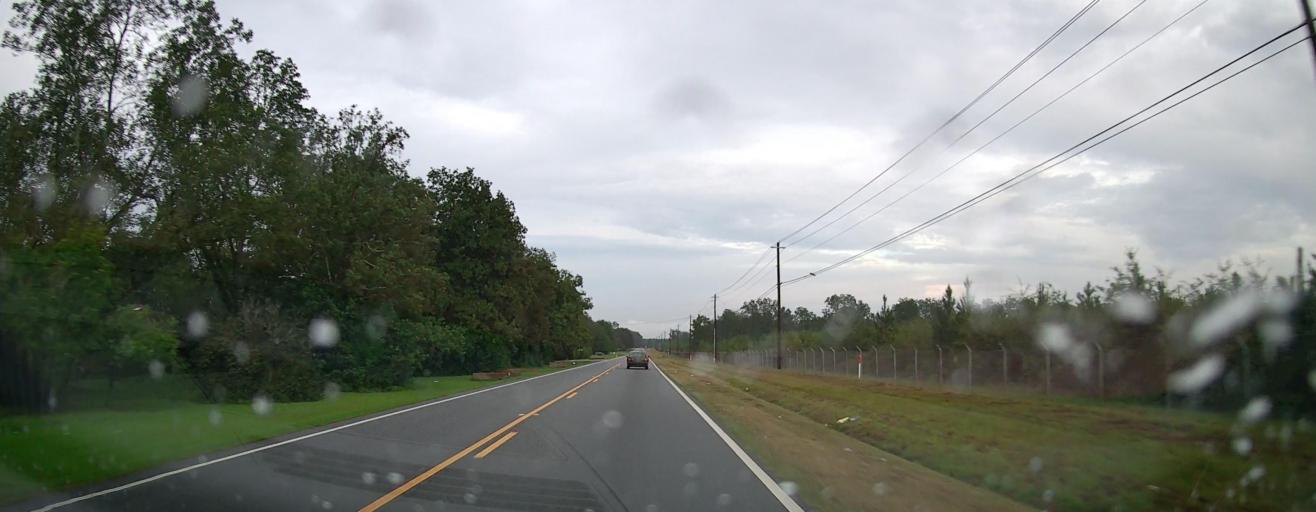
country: US
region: Georgia
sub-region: Peach County
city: Byron
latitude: 32.6655
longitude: -83.7358
